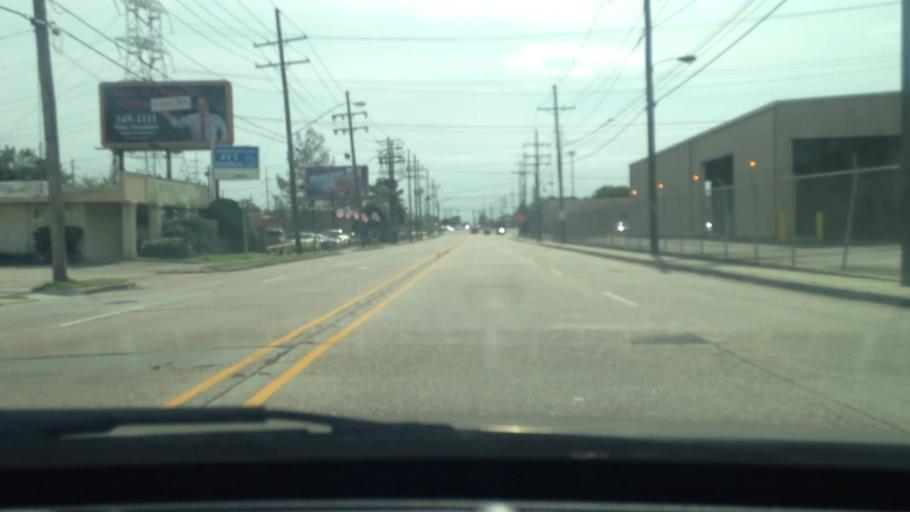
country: US
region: Louisiana
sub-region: Jefferson Parish
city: River Ridge
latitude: 29.9804
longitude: -90.2118
